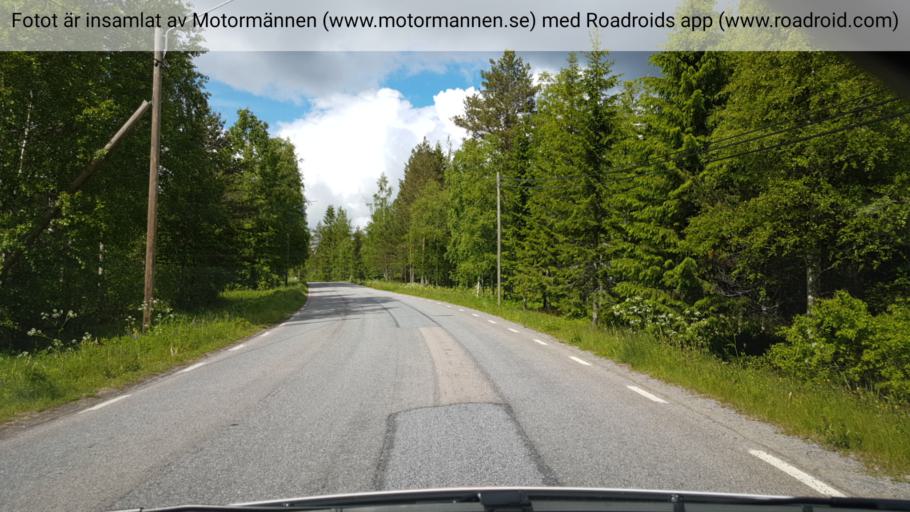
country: SE
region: Vaesterbotten
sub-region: Umea Kommun
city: Hoernefors
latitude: 63.7772
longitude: 19.9913
